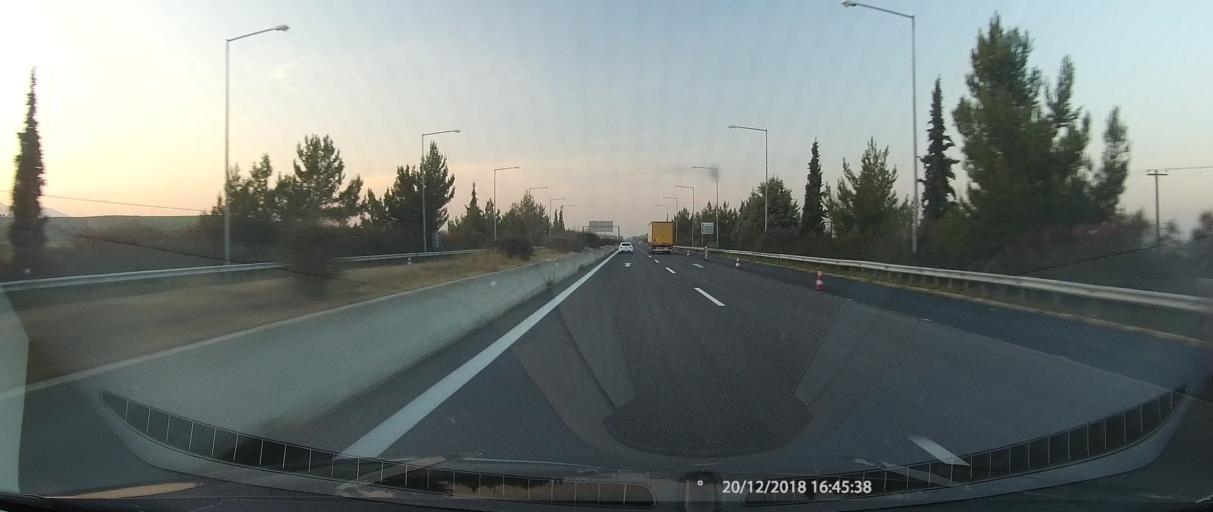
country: GR
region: Thessaly
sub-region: Nomos Magnisias
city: Stefanoviki
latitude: 39.4444
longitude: 22.6858
